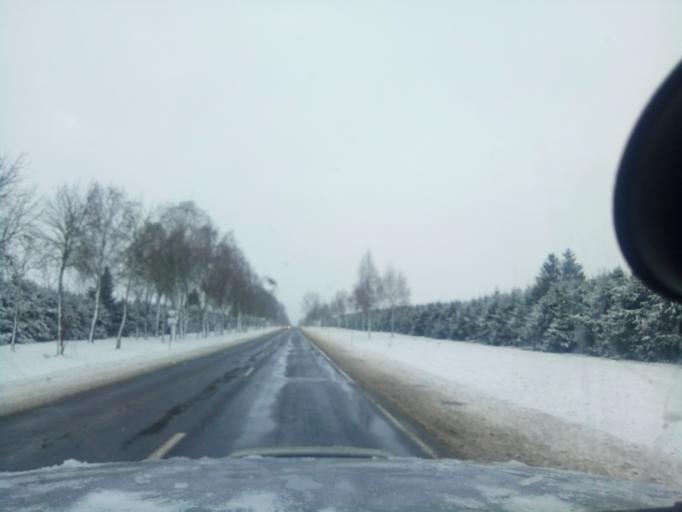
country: BY
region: Minsk
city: Haradzyeya
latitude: 53.3576
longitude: 26.5150
